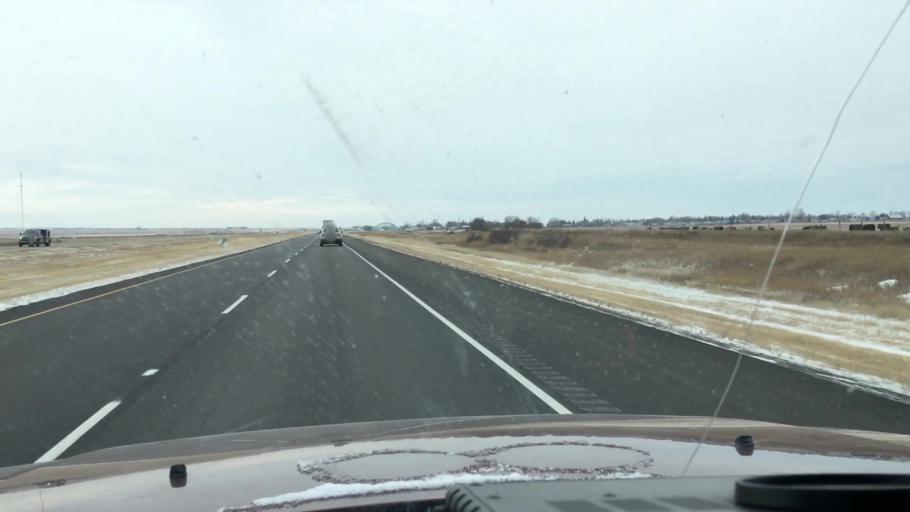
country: CA
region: Saskatchewan
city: Saskatoon
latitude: 51.8258
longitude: -106.5008
